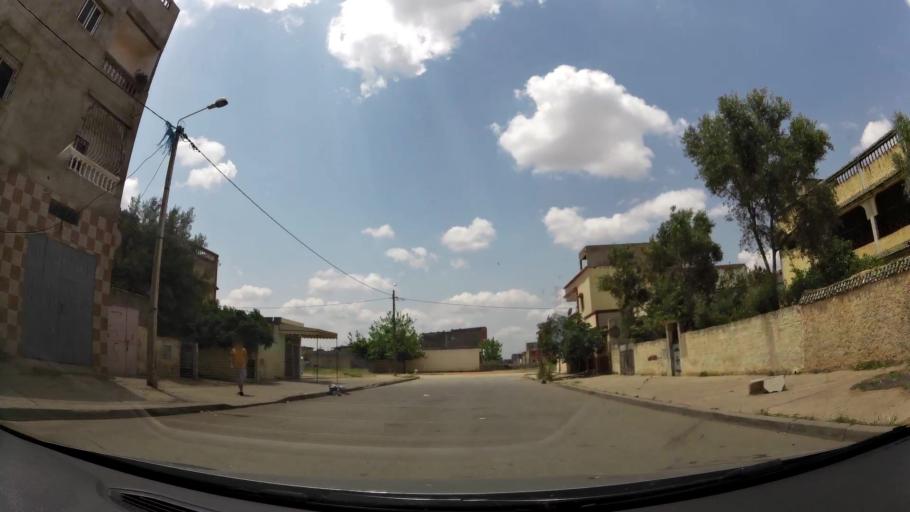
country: MA
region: Rabat-Sale-Zemmour-Zaer
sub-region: Khemisset
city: Tiflet
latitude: 34.0023
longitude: -6.5326
